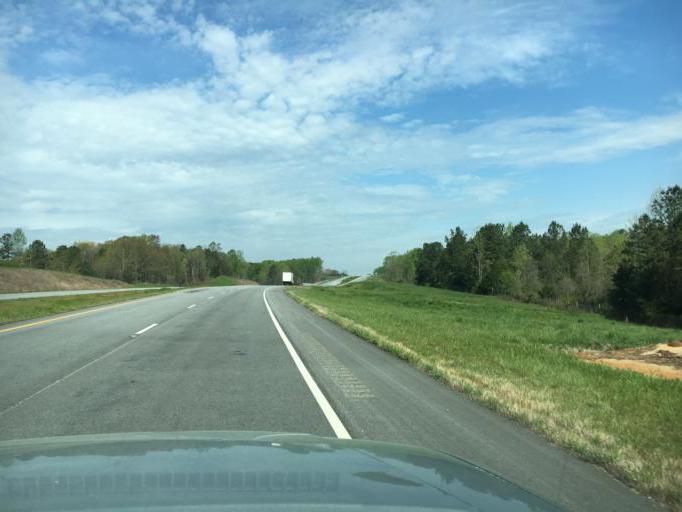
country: US
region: Georgia
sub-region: Franklin County
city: Gumlog
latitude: 34.4951
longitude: -83.1832
